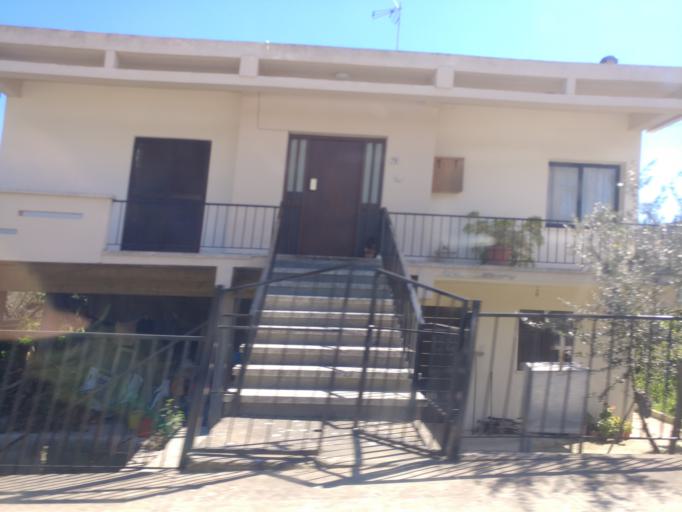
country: CY
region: Pafos
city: Tala
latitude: 34.9227
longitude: 32.4777
